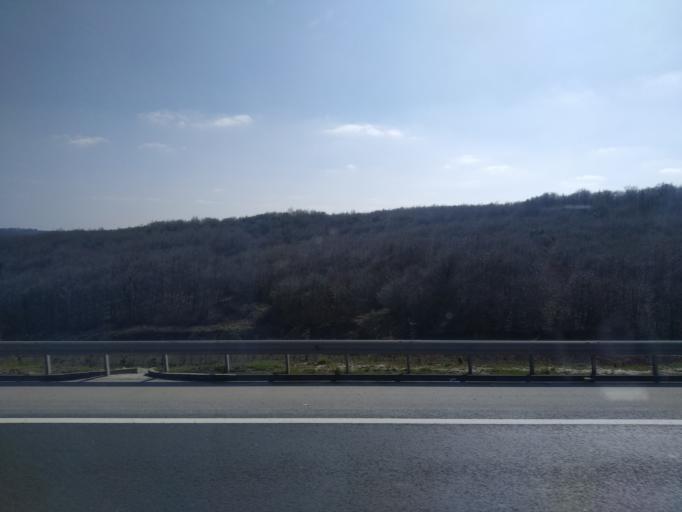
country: TR
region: Istanbul
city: Kemerburgaz
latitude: 41.2313
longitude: 28.8686
